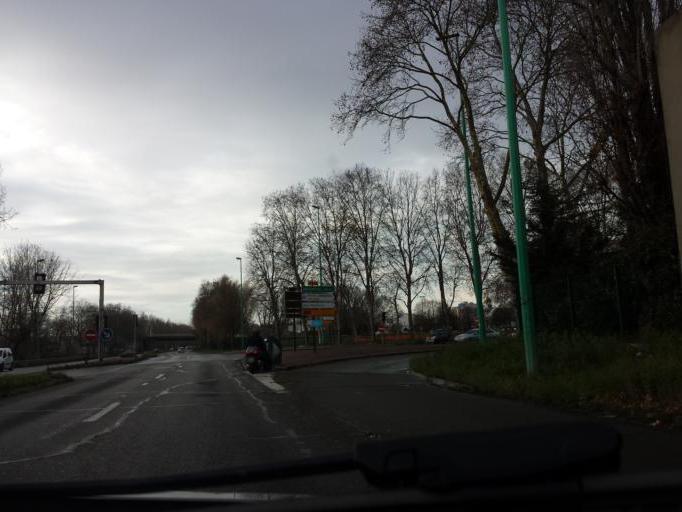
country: FR
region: Ile-de-France
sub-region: Departement du Val-d'Oise
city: Argenteuil
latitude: 48.9429
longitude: 2.2573
